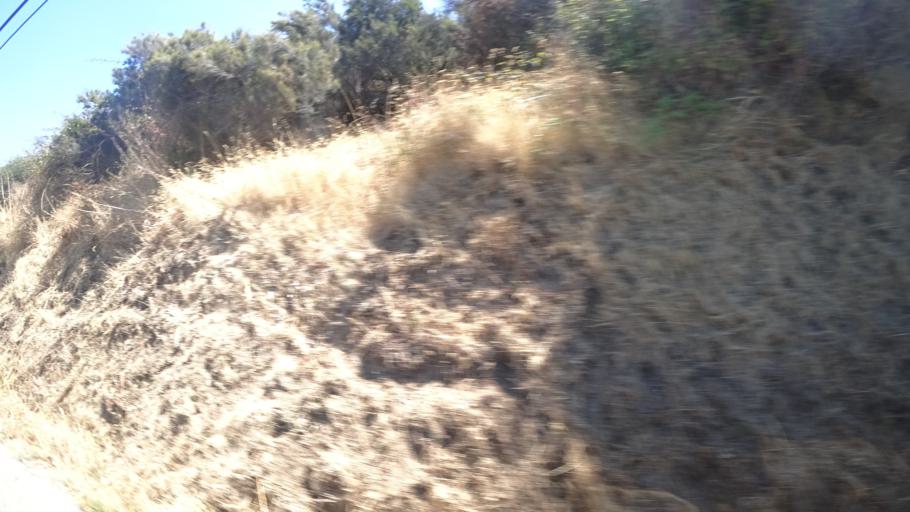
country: FR
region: Corsica
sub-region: Departement de la Corse-du-Sud
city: Alata
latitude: 41.9804
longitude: 8.6779
